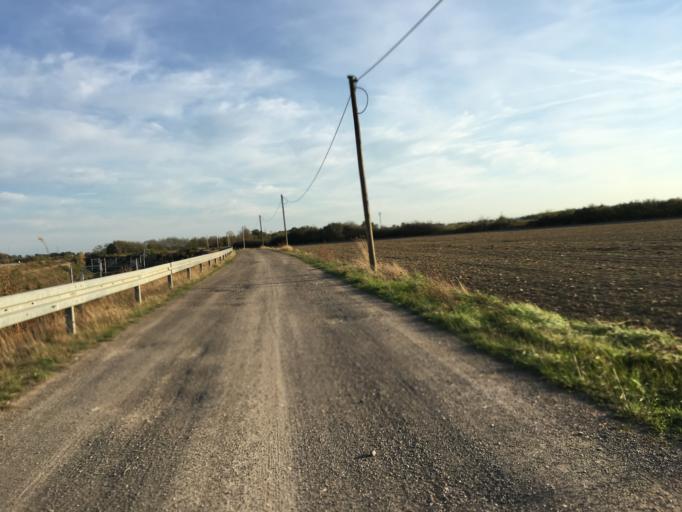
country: DE
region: North Rhine-Westphalia
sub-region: Regierungsbezirk Koln
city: Merzenich
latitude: 50.8551
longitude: 6.5176
